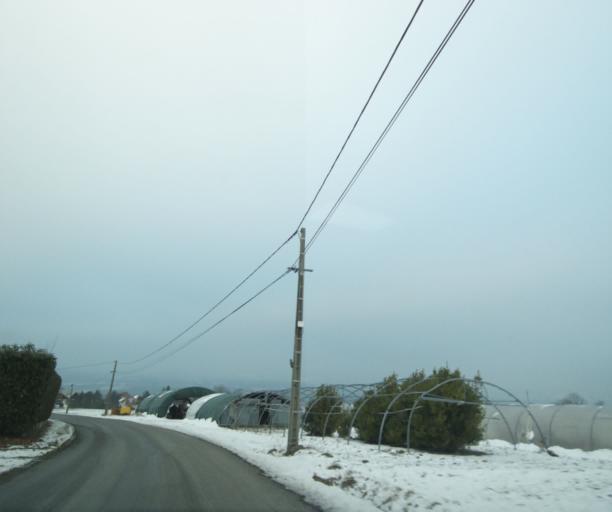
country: FR
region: Rhone-Alpes
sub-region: Departement de la Haute-Savoie
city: Reignier-Esery
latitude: 46.1315
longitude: 6.2480
